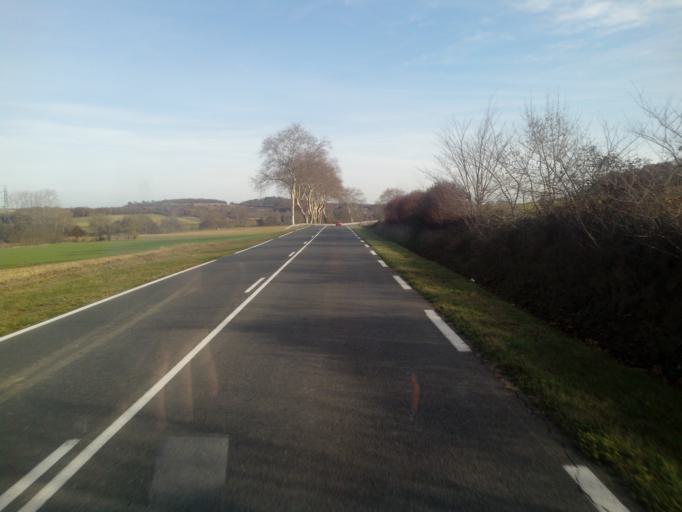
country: FR
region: Languedoc-Roussillon
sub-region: Departement de l'Aude
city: Villepinte
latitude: 43.2888
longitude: 2.0623
